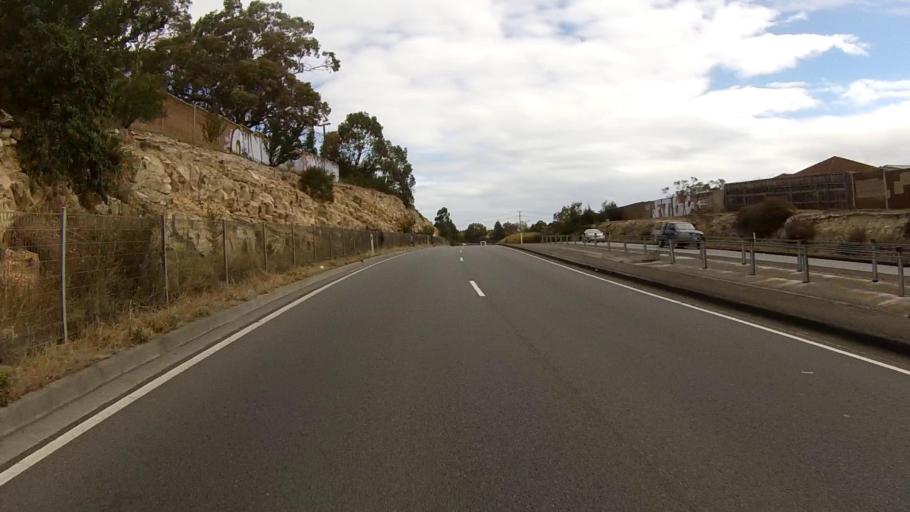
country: AU
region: Tasmania
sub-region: Clarence
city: Howrah
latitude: -42.8821
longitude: 147.4104
